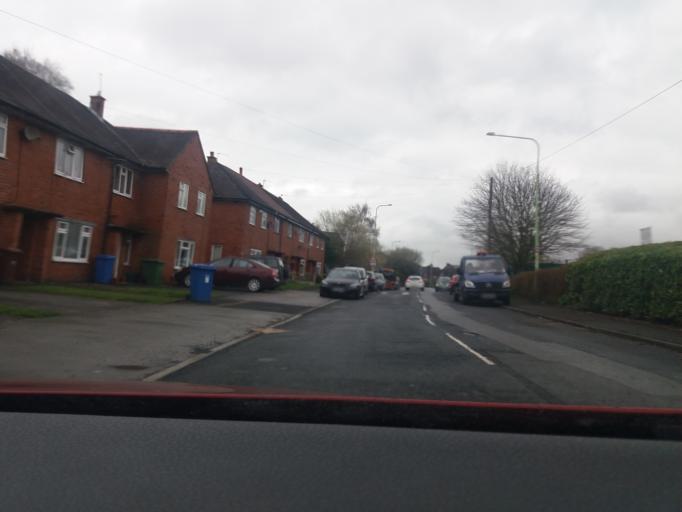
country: GB
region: England
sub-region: Lancashire
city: Chorley
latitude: 53.6400
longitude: -2.6374
